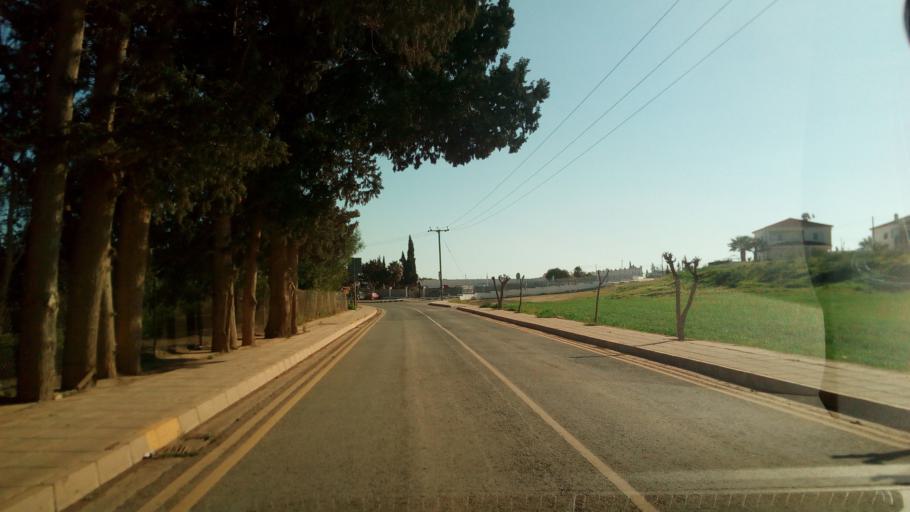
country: CY
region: Ammochostos
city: Avgorou
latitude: 35.0389
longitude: 33.8436
